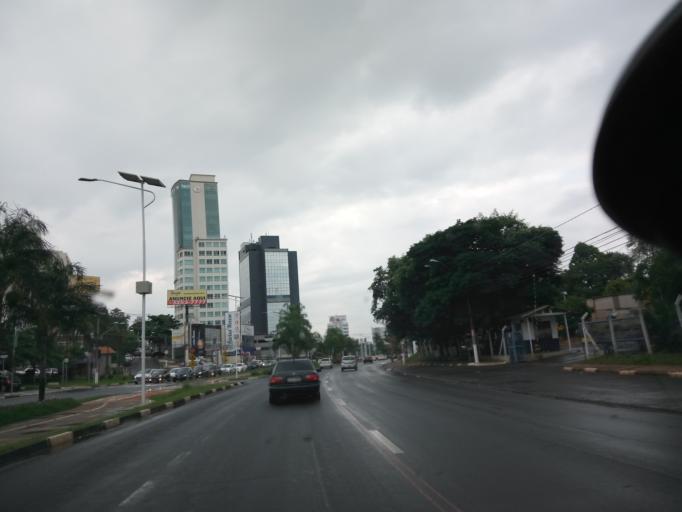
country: BR
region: Sao Paulo
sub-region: Campinas
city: Campinas
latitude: -22.8921
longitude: -47.0471
